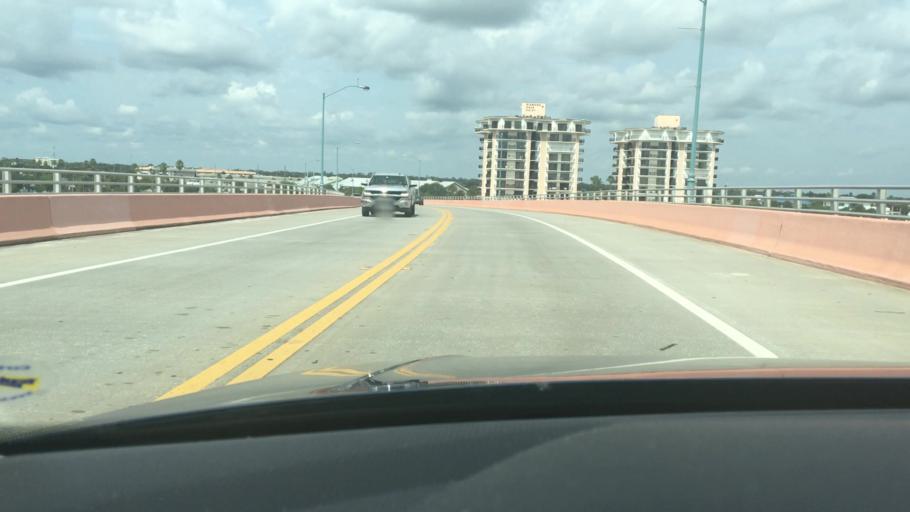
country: US
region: Florida
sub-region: Volusia County
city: New Smyrna Beach
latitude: 29.0388
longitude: -80.9060
